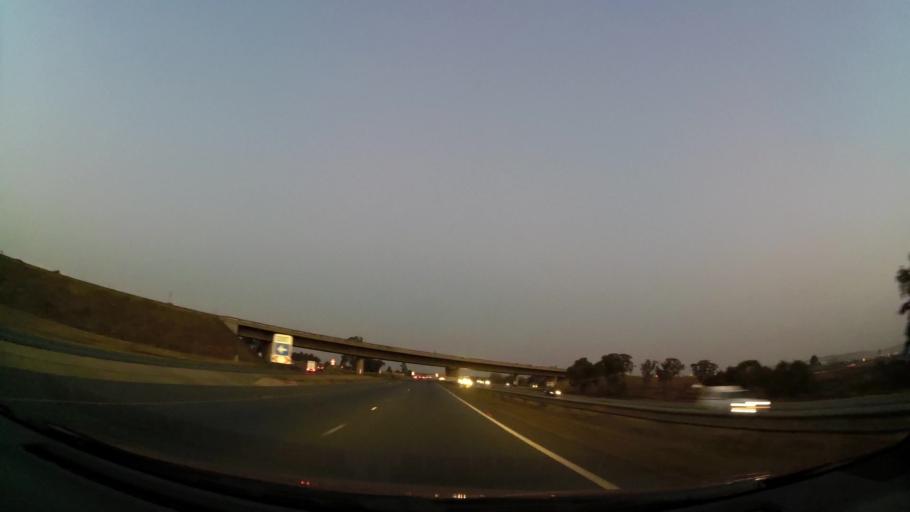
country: ZA
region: Gauteng
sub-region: City of Johannesburg Metropolitan Municipality
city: Soweto
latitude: -26.2969
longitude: 27.8462
